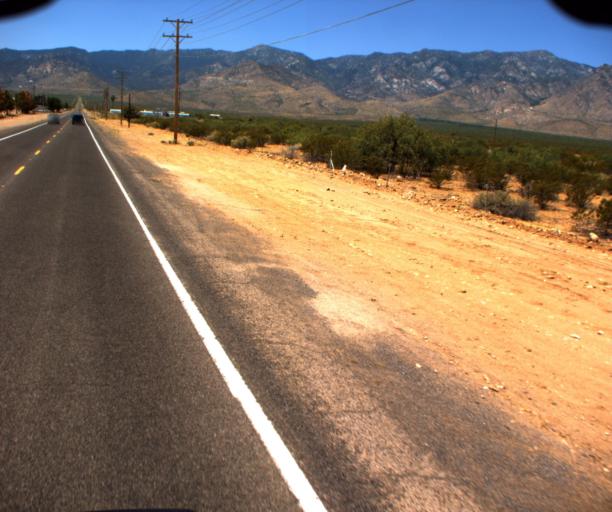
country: US
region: Arizona
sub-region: Graham County
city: Swift Trail Junction
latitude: 32.7225
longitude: -109.7217
